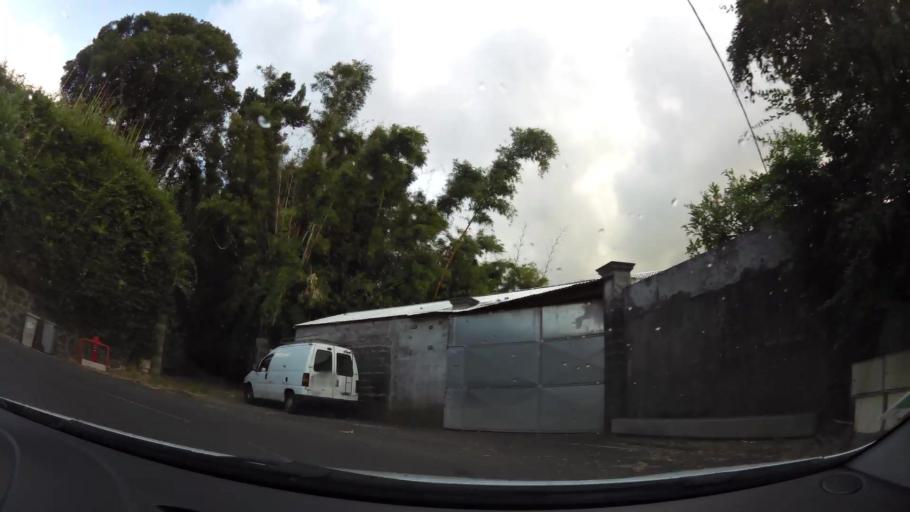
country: RE
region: Reunion
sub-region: Reunion
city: Saint-Denis
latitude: -20.9161
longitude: 55.4391
